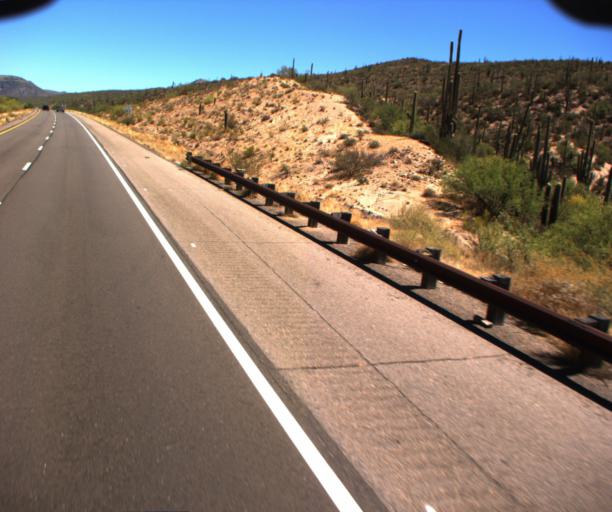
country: US
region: Arizona
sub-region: Maricopa County
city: Rio Verde
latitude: 33.7617
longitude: -111.4947
